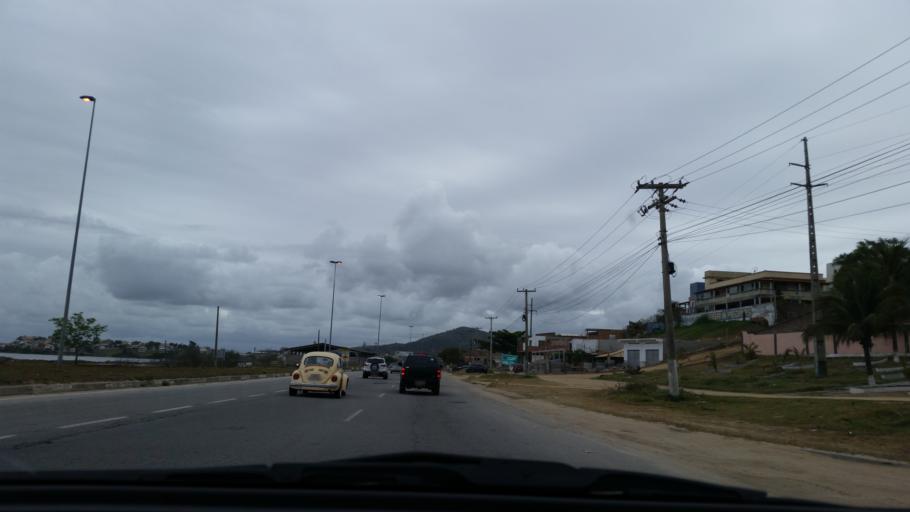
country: BR
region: Rio de Janeiro
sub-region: Sao Pedro Da Aldeia
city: Sao Pedro da Aldeia
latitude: -22.8538
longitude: -42.0614
